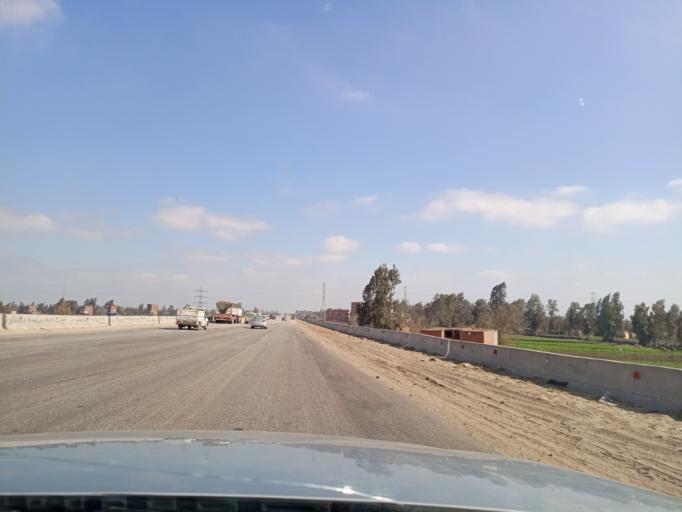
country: EG
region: Muhafazat al Minufiyah
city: Al Bajur
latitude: 30.4359
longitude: 31.1062
